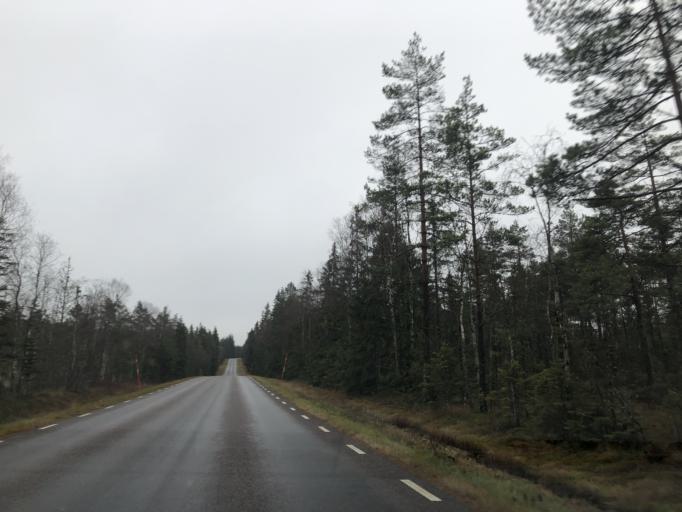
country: SE
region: Vaestra Goetaland
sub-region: Ulricehamns Kommun
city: Ulricehamn
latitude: 57.7428
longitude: 13.5364
